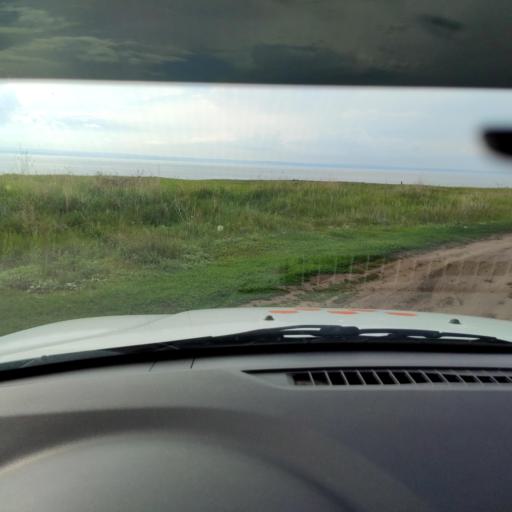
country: RU
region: Samara
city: Podstepki
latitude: 53.6105
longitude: 49.0298
